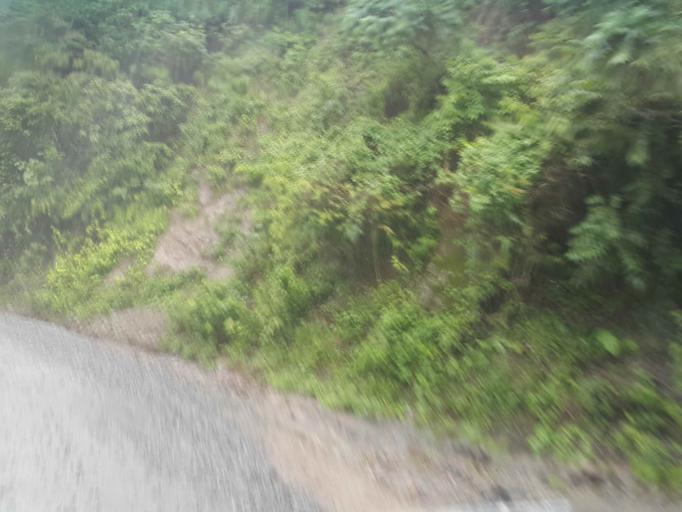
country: CR
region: Guanacaste
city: Juntas
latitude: 10.2465
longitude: -84.8412
